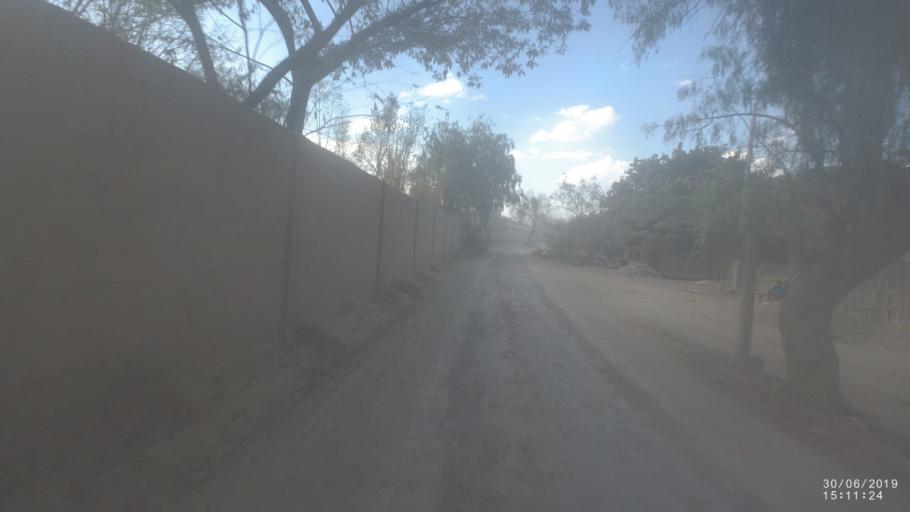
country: BO
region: Cochabamba
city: Irpa Irpa
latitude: -17.7284
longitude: -66.2922
